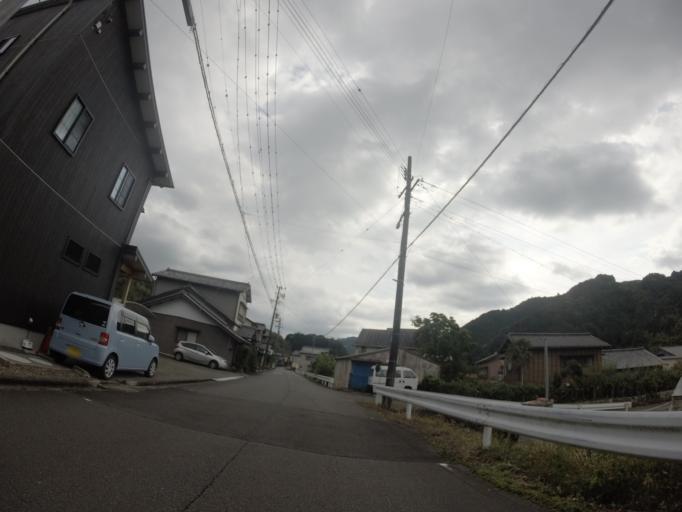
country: JP
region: Shizuoka
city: Fujieda
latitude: 34.9095
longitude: 138.1945
